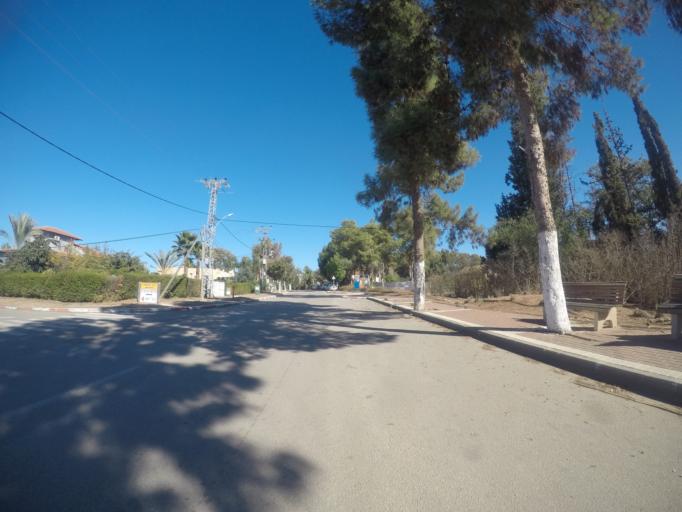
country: IL
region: Southern District
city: Qiryat Gat
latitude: 31.6202
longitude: 34.7021
